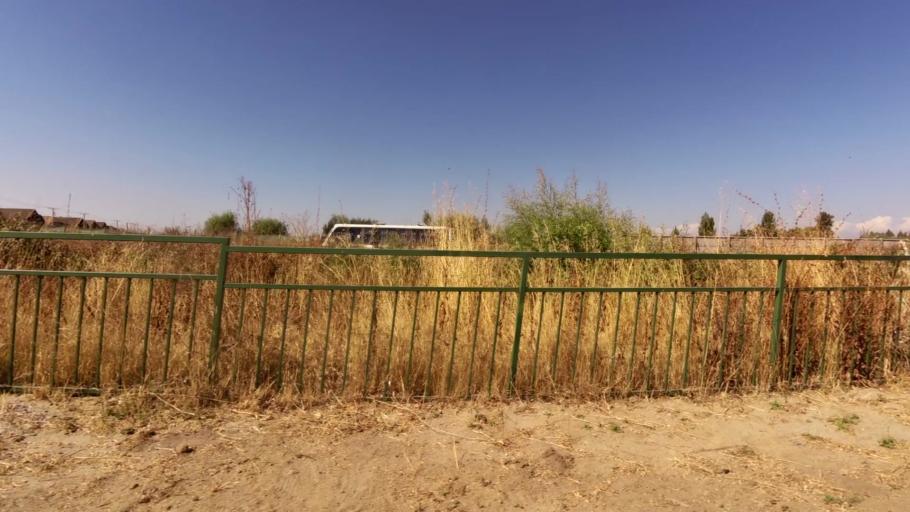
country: CL
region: Maule
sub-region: Provincia de Talca
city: Talca
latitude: -35.4205
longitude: -71.6098
